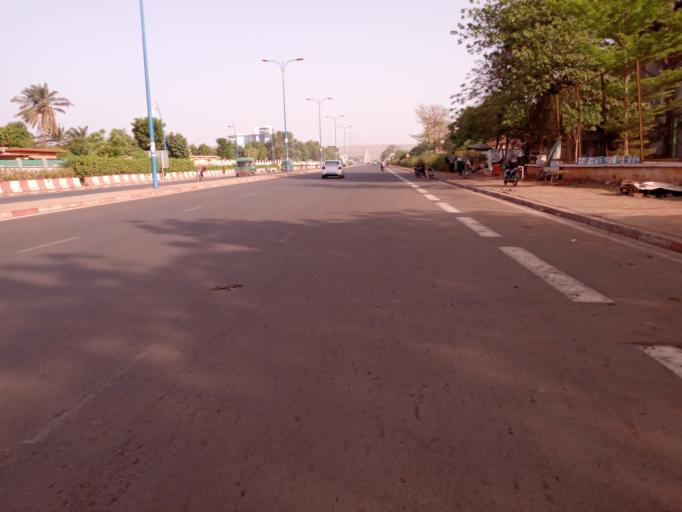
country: ML
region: Bamako
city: Bamako
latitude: 12.6318
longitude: -8.0014
